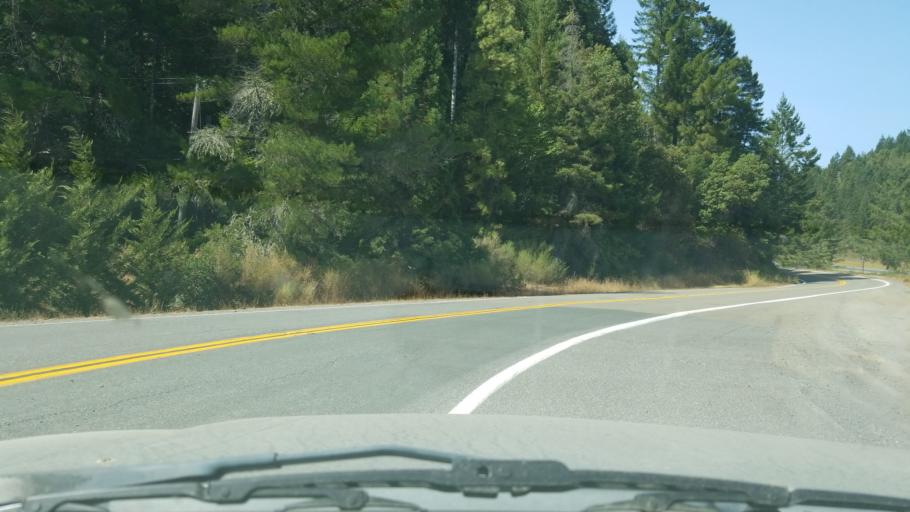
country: US
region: California
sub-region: Mendocino County
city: Laytonville
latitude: 39.8481
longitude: -123.7087
